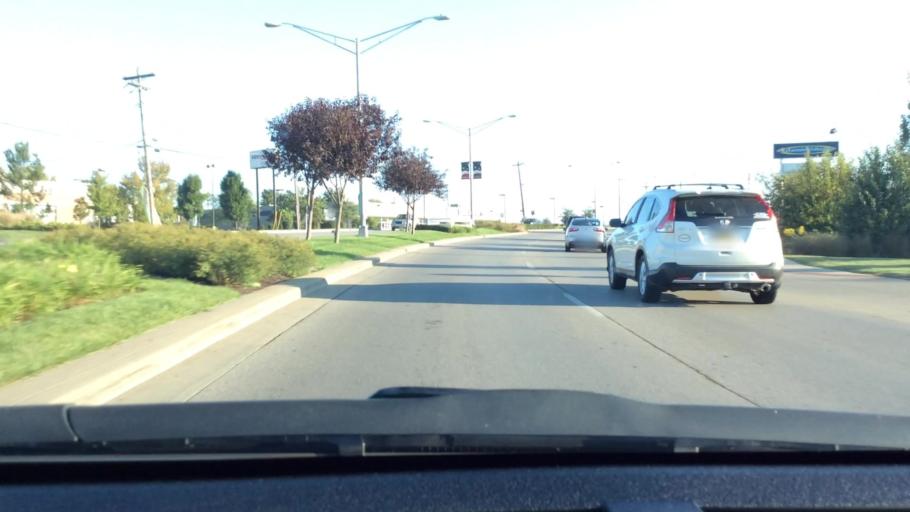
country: US
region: Kentucky
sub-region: Boone County
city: Florence
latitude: 39.0013
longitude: -84.6533
